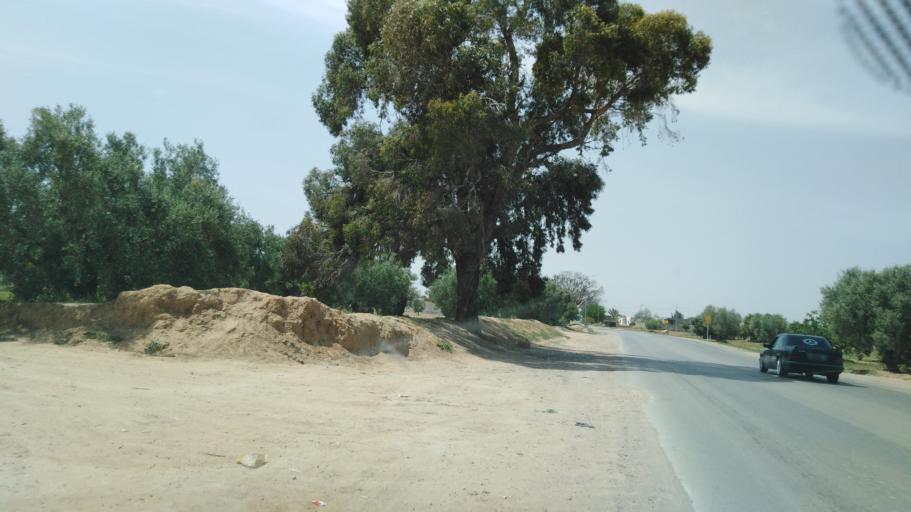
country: TN
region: Safaqis
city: Sfax
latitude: 34.7323
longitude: 10.5563
